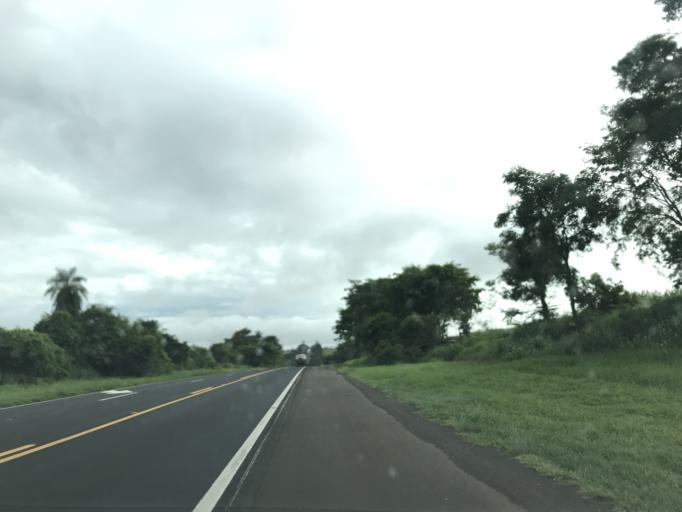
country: BR
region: Sao Paulo
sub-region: Penapolis
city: Penapolis
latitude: -21.4625
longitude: -50.1769
